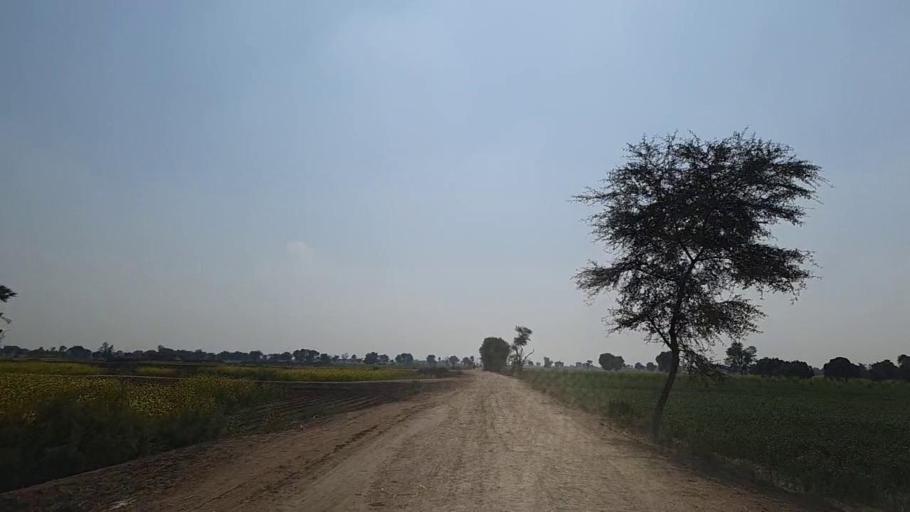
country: PK
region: Sindh
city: Daur
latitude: 26.4542
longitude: 68.2631
